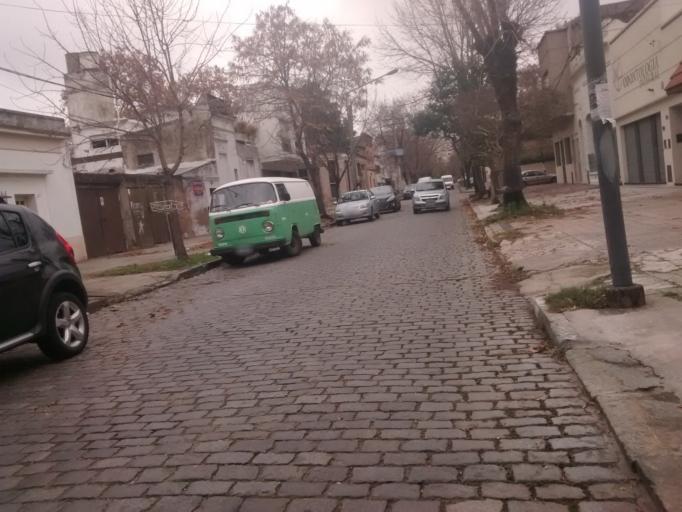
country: AR
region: Buenos Aires
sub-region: Partido de La Plata
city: La Plata
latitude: -34.8986
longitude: -57.9523
